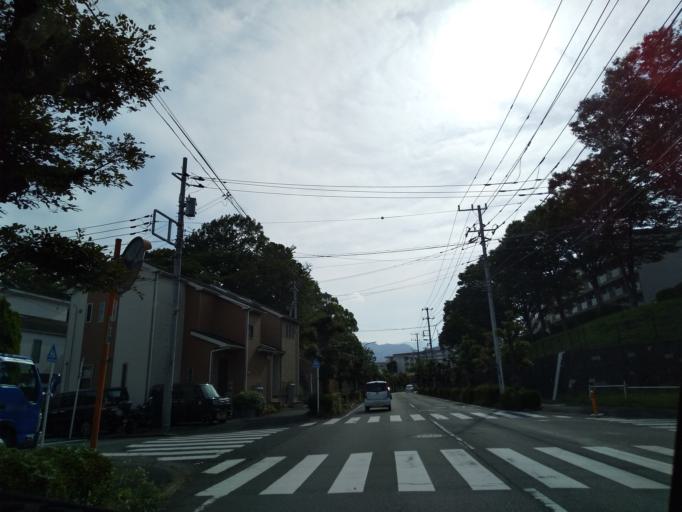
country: JP
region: Kanagawa
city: Zama
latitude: 35.4914
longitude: 139.3313
